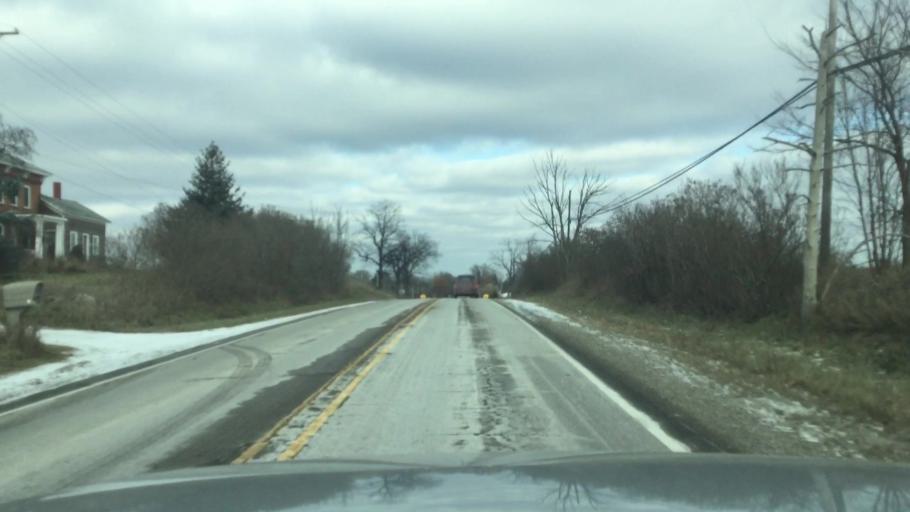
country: US
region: Michigan
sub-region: Genesee County
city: Linden
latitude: 42.8367
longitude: -83.7830
